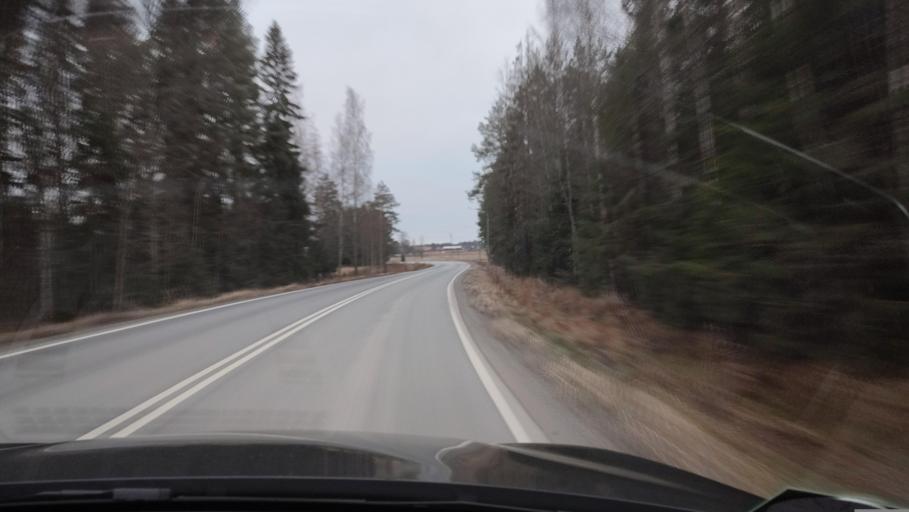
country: FI
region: Southern Ostrobothnia
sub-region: Suupohja
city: Karijoki
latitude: 62.2722
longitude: 21.5642
